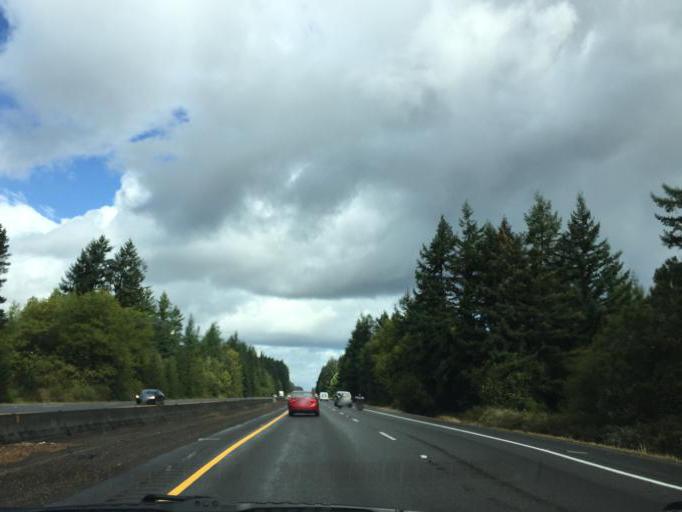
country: US
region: Washington
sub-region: Lewis County
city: Winlock
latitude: 46.5057
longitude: -122.8766
